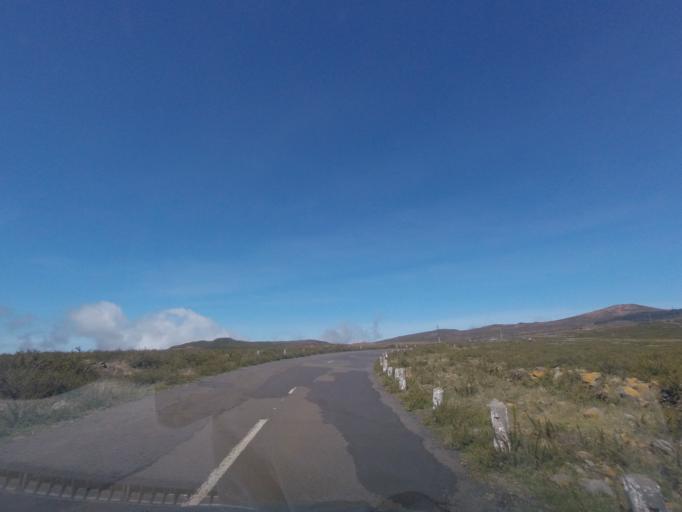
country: PT
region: Madeira
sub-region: Calheta
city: Arco da Calheta
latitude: 32.7528
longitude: -17.0989
